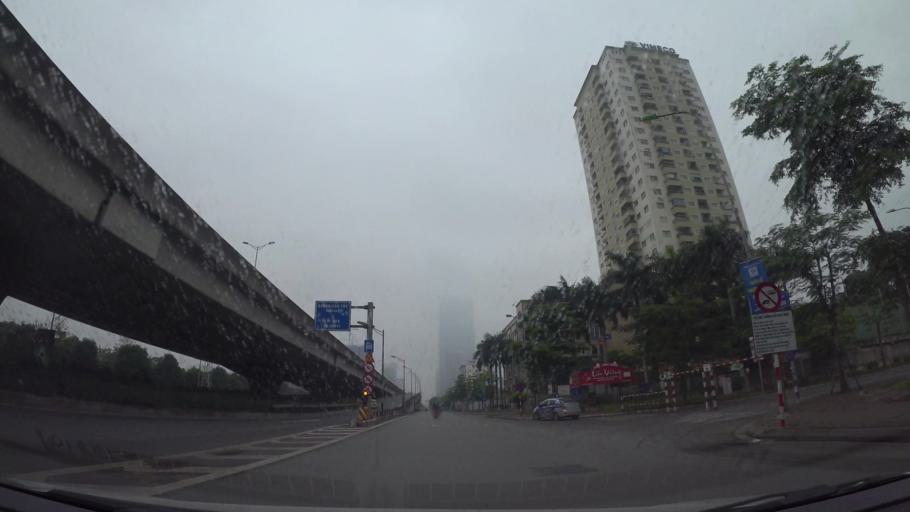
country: VN
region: Ha Noi
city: Thanh Xuan
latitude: 21.0078
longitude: 105.7904
